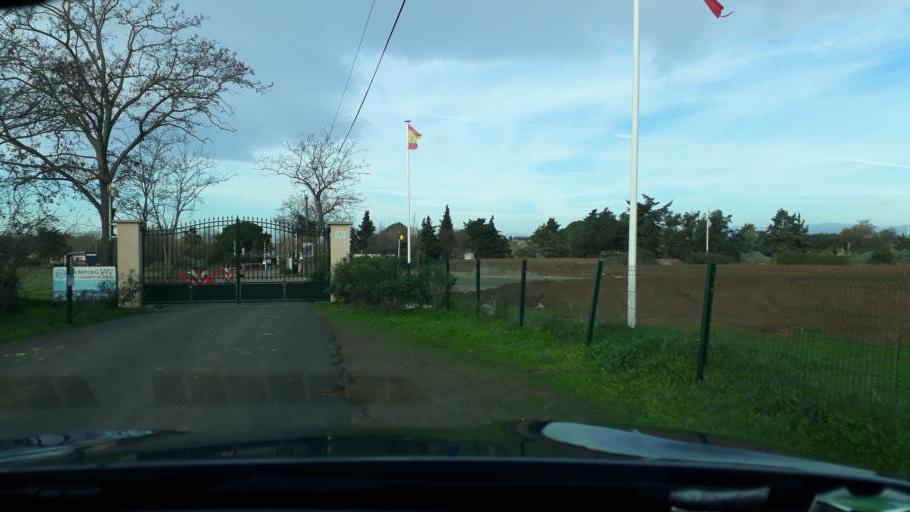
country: FR
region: Languedoc-Roussillon
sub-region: Departement de l'Herault
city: Agde
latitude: 43.2961
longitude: 3.4783
